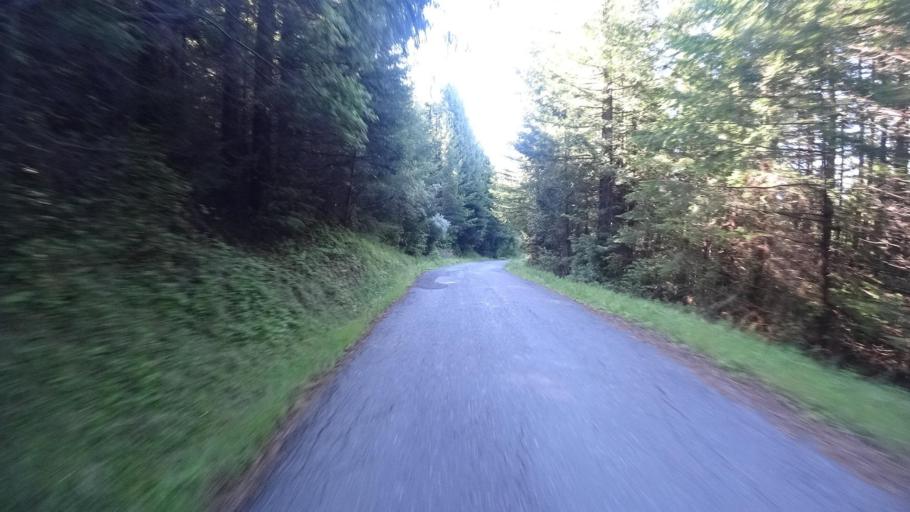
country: US
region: California
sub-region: Humboldt County
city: Rio Dell
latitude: 40.4483
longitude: -123.9772
